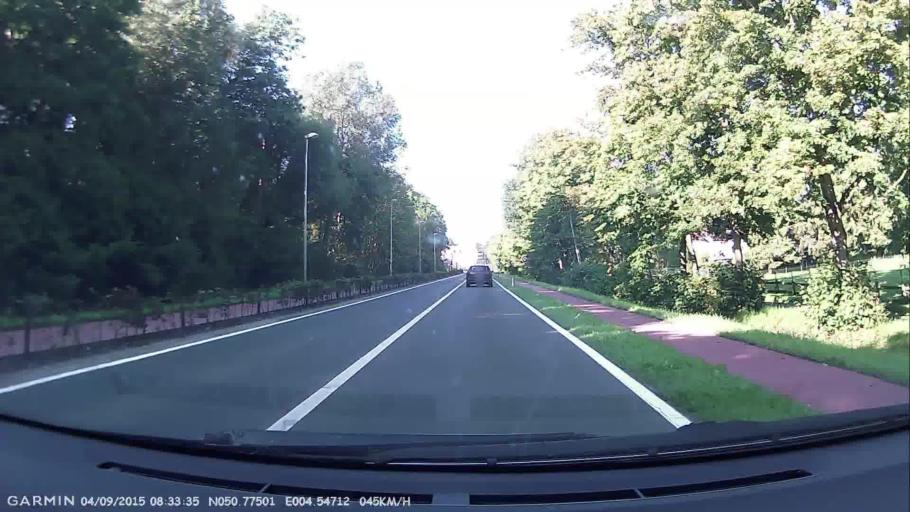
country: BE
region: Flanders
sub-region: Provincie Vlaams-Brabant
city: Overijse
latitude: 50.7749
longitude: 4.5468
